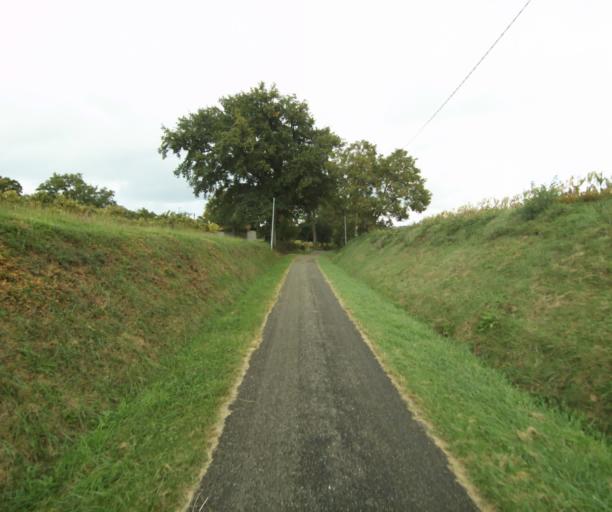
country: FR
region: Midi-Pyrenees
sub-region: Departement du Gers
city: Cazaubon
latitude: 43.8686
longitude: -0.0316
